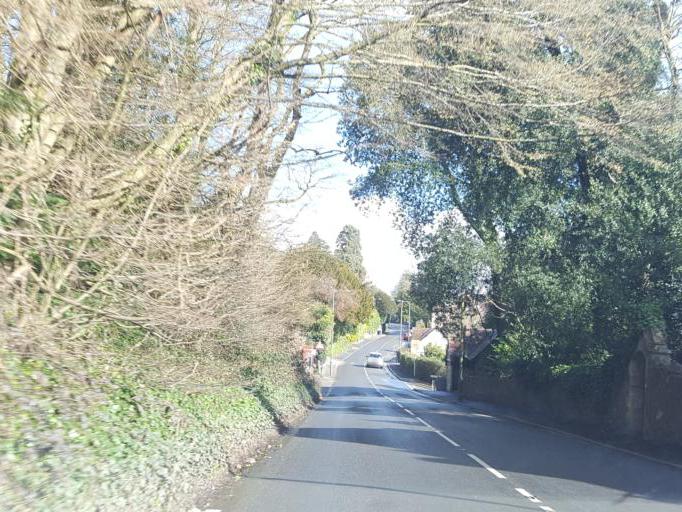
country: GB
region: England
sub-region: Worcestershire
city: Great Malvern
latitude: 52.0701
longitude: -2.3344
